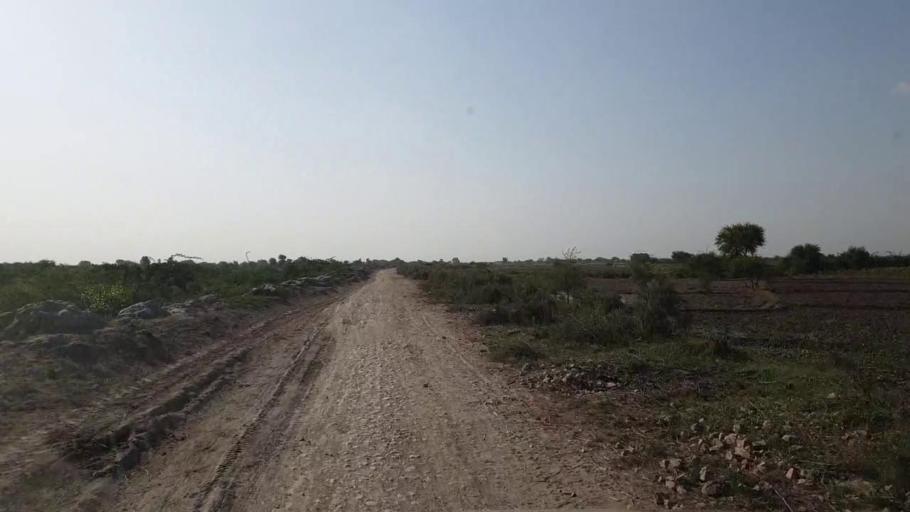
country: PK
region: Sindh
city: Kadhan
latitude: 24.6275
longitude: 69.0732
